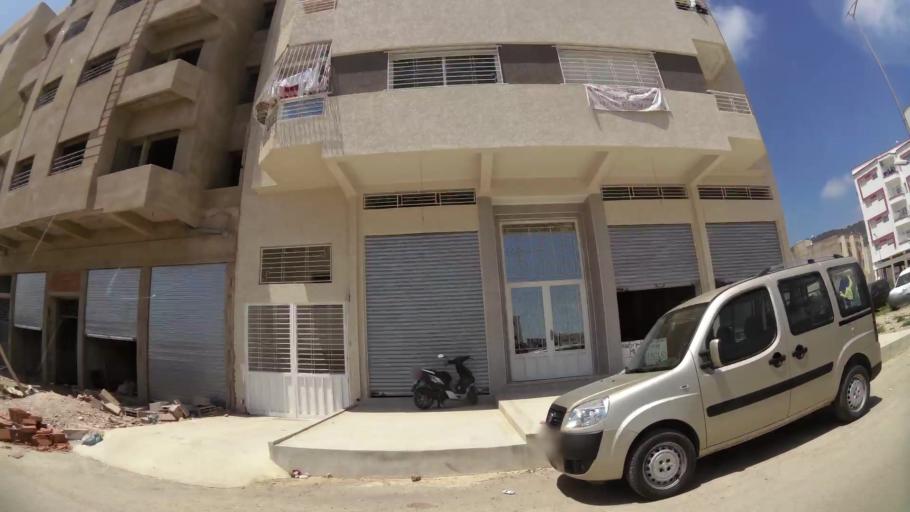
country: MA
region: Fes-Boulemane
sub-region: Fes
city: Fes
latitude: 34.0517
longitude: -5.0410
